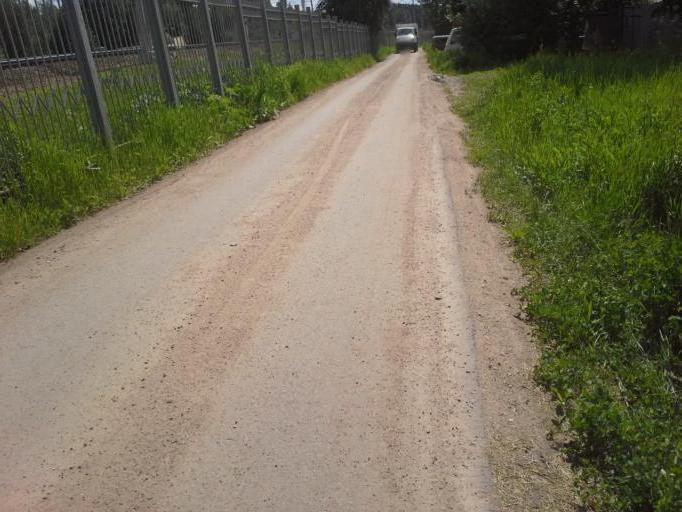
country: RU
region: Moskovskaya
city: Lesnoy Gorodok
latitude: 55.6274
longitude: 37.2163
